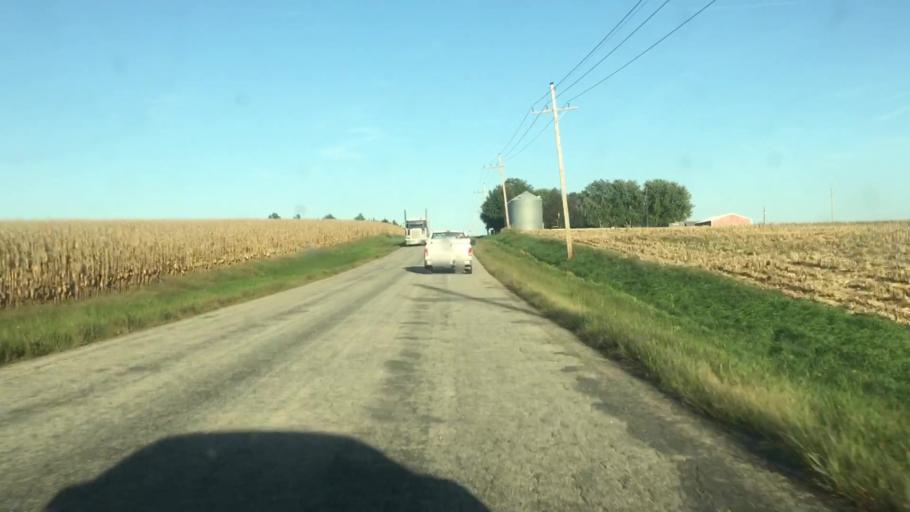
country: US
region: Kansas
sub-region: Brown County
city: Horton
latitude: 39.5656
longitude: -95.3626
